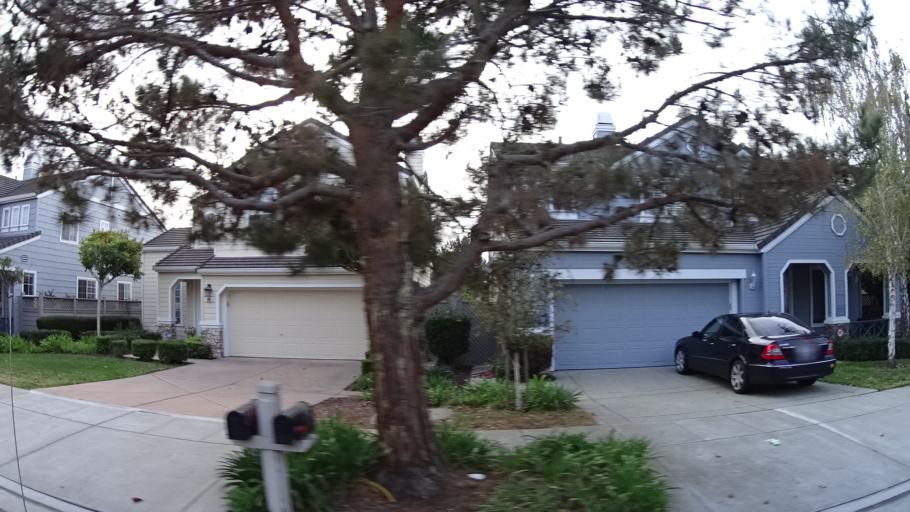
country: US
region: California
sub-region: San Mateo County
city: Redwood Shores
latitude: 37.5422
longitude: -122.2432
